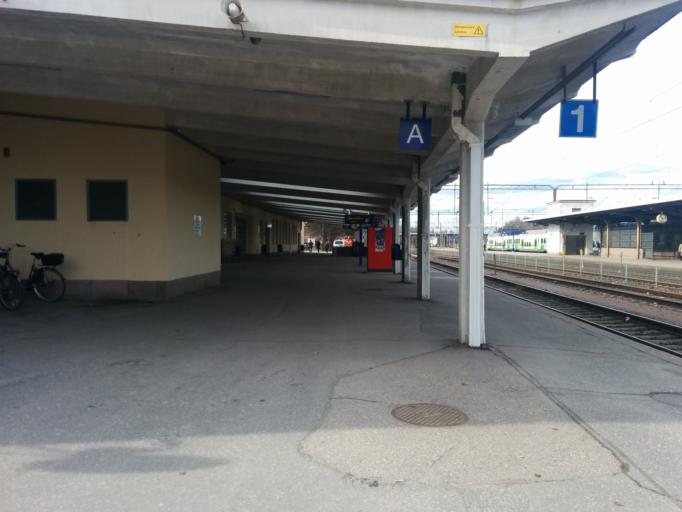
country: FI
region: Haeme
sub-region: Riihimaeki
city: Riihimaeki
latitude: 60.7347
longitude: 24.7815
